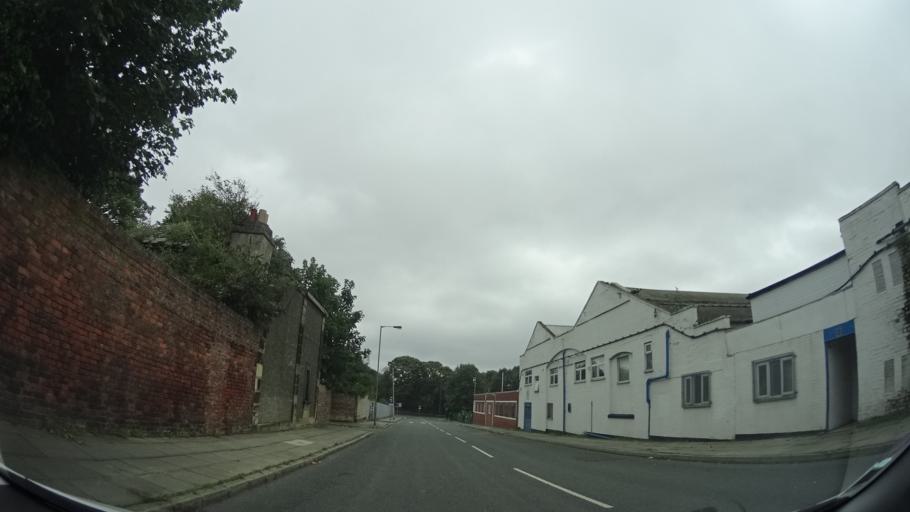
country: GB
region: England
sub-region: Liverpool
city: Liverpool
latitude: 53.4097
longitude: -2.9423
